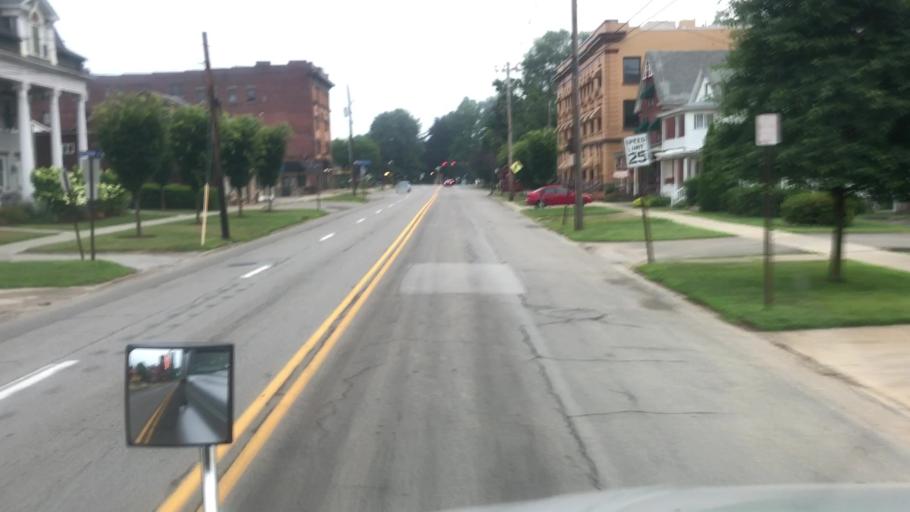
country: US
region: Pennsylvania
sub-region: Venango County
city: Franklin
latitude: 41.3954
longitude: -79.8267
